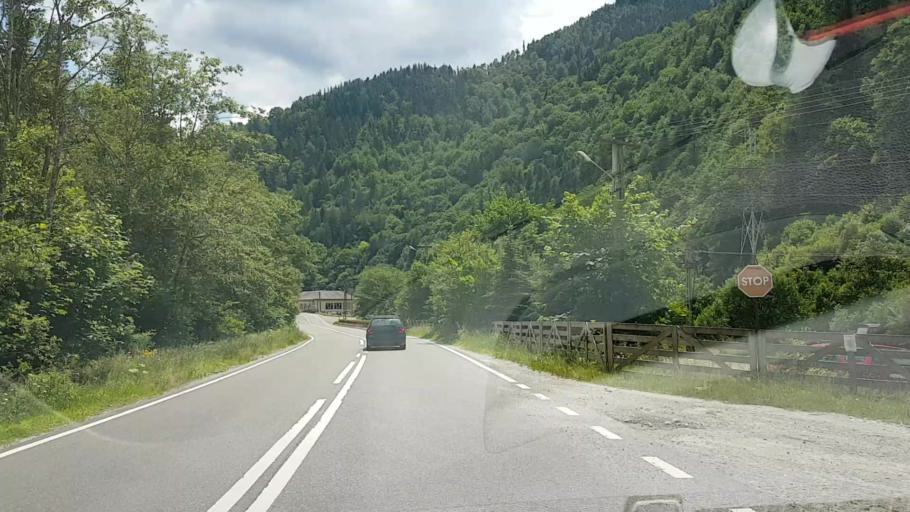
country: RO
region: Suceava
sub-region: Comuna Crucea
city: Crucea
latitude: 47.2861
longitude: 25.6356
